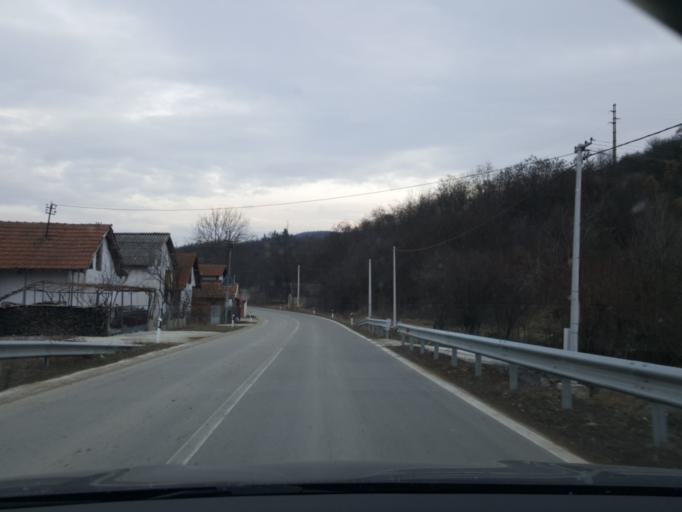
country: RS
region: Central Serbia
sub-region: Pirotski Okrug
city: Pirot
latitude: 43.1915
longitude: 22.5611
